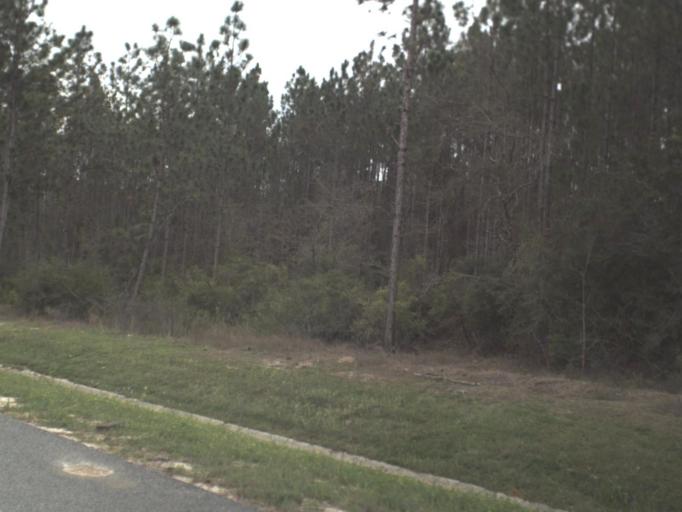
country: US
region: Florida
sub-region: Gulf County
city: Wewahitchka
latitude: 30.2506
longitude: -85.2293
